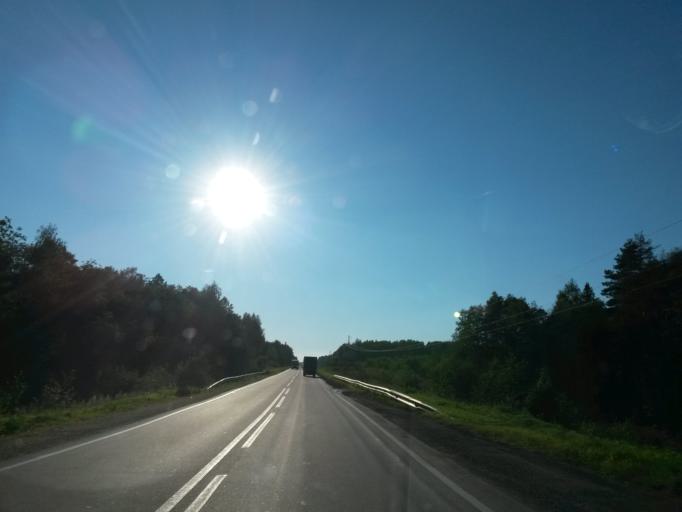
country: RU
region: Jaroslavl
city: Dubki
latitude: 57.2585
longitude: 40.0726
